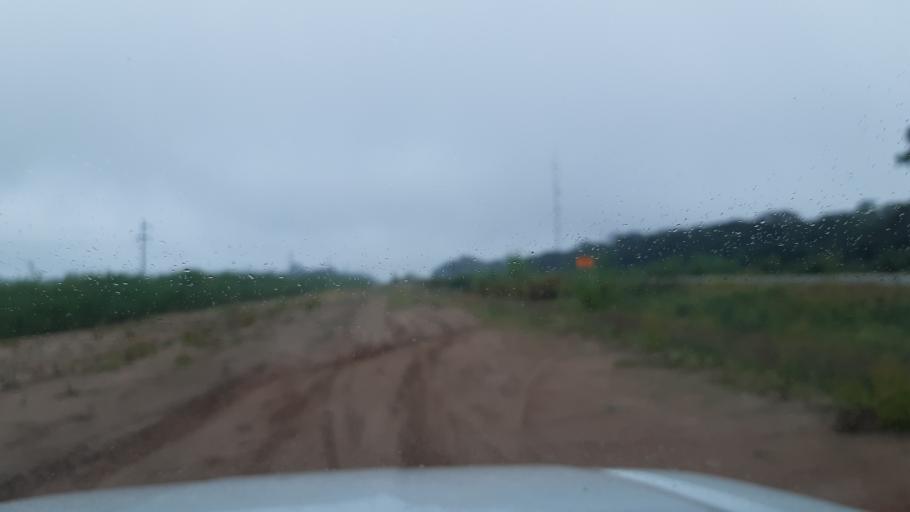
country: AR
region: Jujuy
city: La Mendieta
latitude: -24.3755
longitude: -65.0083
